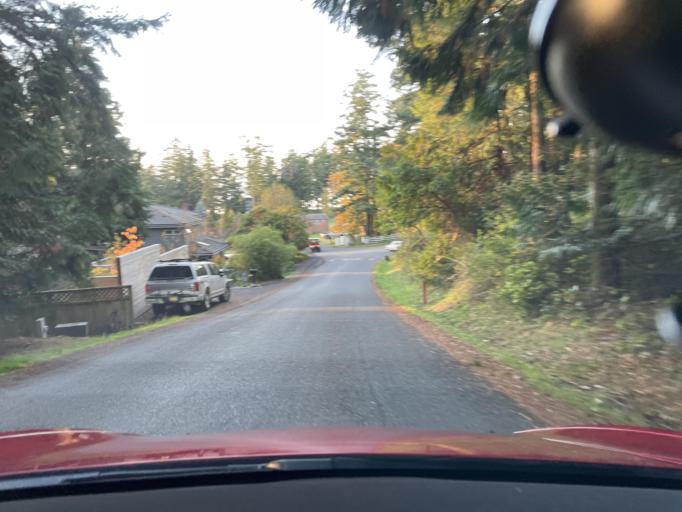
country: US
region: Washington
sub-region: San Juan County
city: Friday Harbor
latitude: 48.6137
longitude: -123.1539
